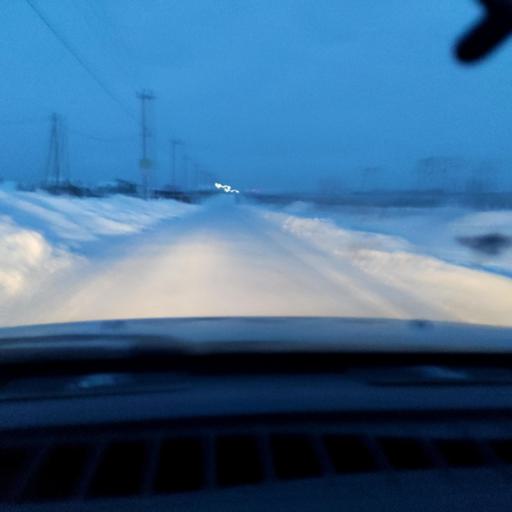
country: RU
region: Perm
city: Kultayevo
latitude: 57.8737
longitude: 55.9819
